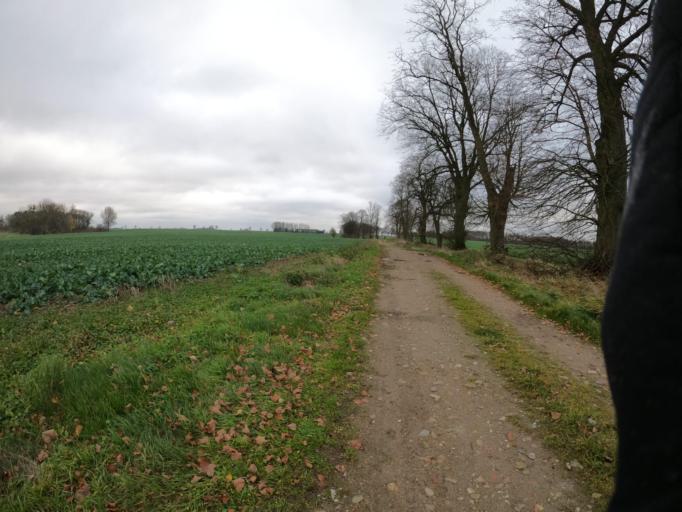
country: PL
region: West Pomeranian Voivodeship
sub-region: Powiat walecki
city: Tuczno
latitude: 53.2742
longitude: 16.1715
